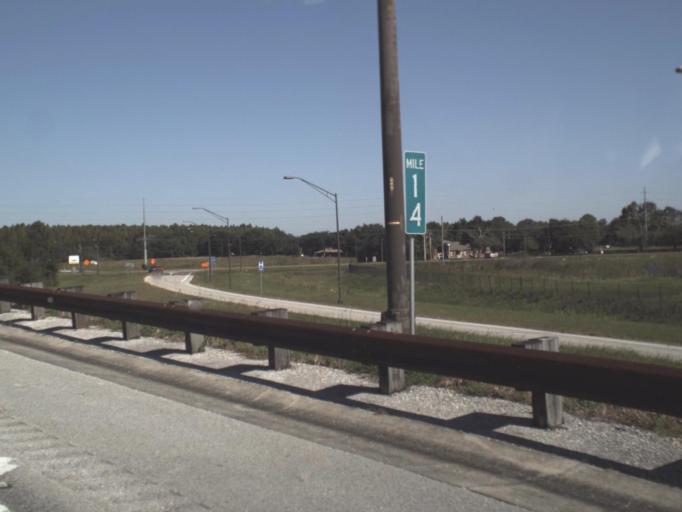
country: US
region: Florida
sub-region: Hillsborough County
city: Greater Northdale
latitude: 28.1261
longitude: -82.5474
